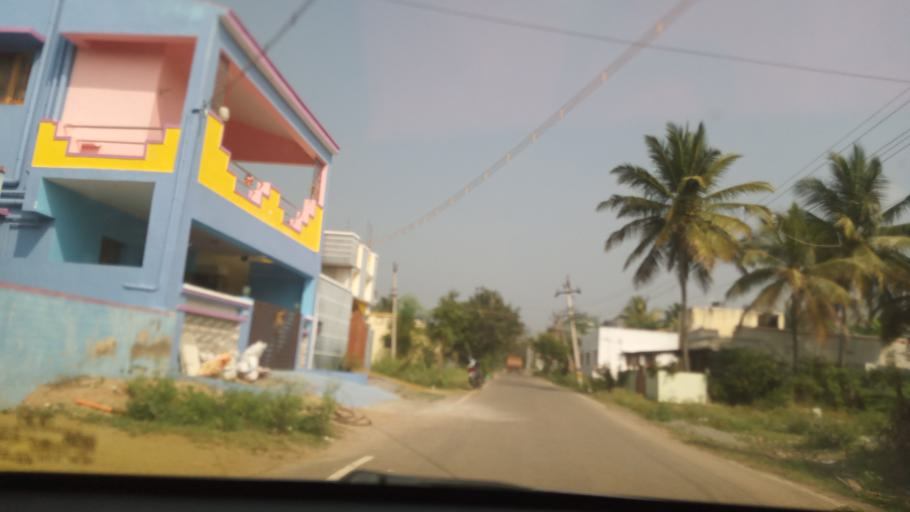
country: IN
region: Tamil Nadu
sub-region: Coimbatore
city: Perur
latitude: 11.0058
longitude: 76.8900
